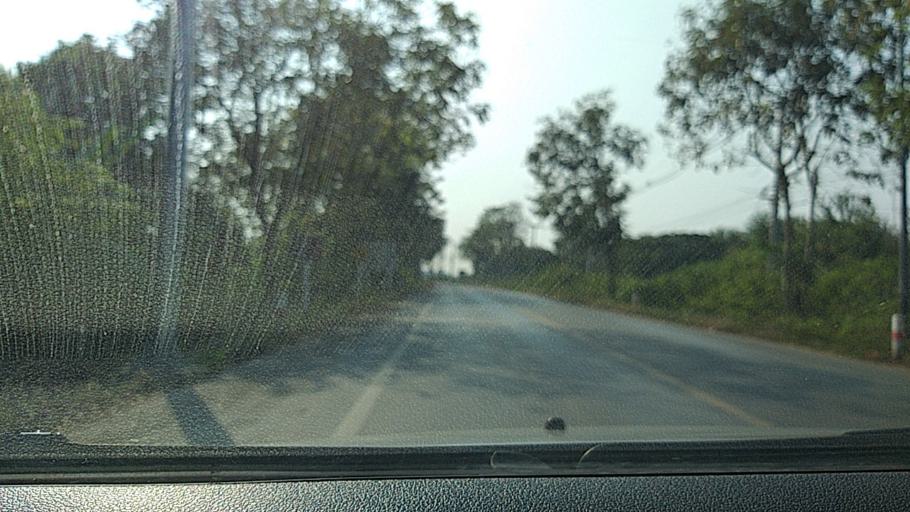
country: TH
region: Ang Thong
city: Chaiyo
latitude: 14.7238
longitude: 100.4544
